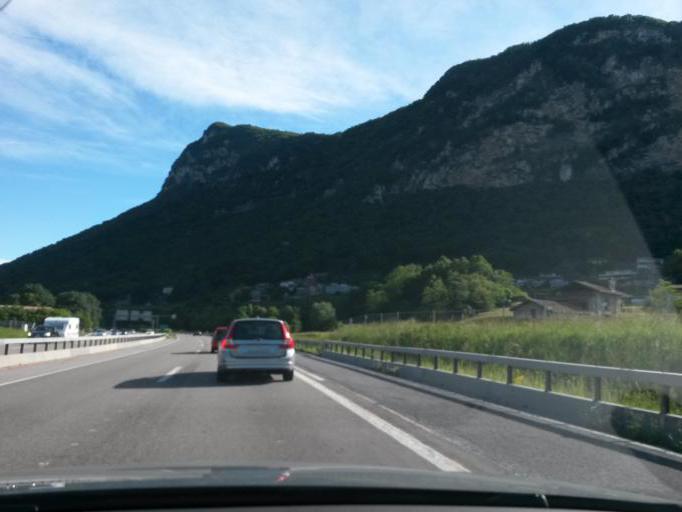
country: CH
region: Ticino
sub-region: Mendrisio District
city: Mendrisio
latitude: 45.8781
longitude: 8.9801
